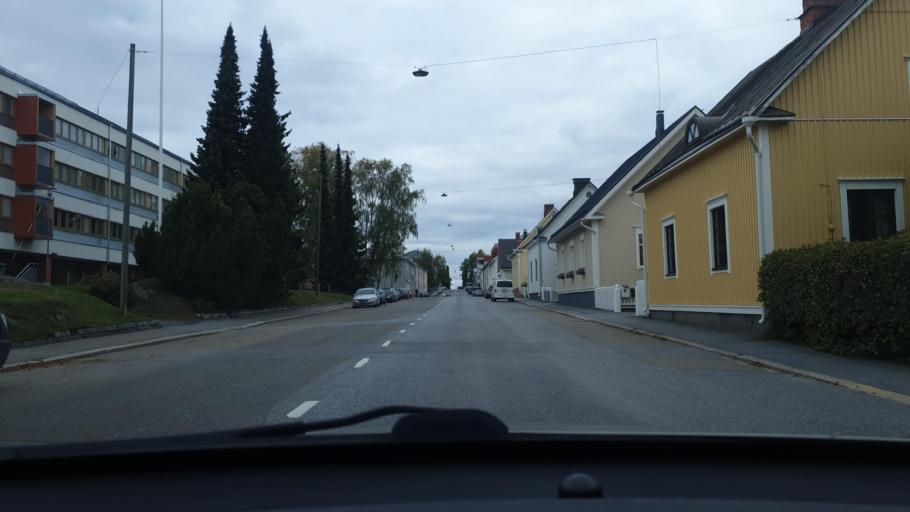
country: FI
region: Ostrobothnia
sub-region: Vaasa
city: Vaasa
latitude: 63.0874
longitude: 21.6297
